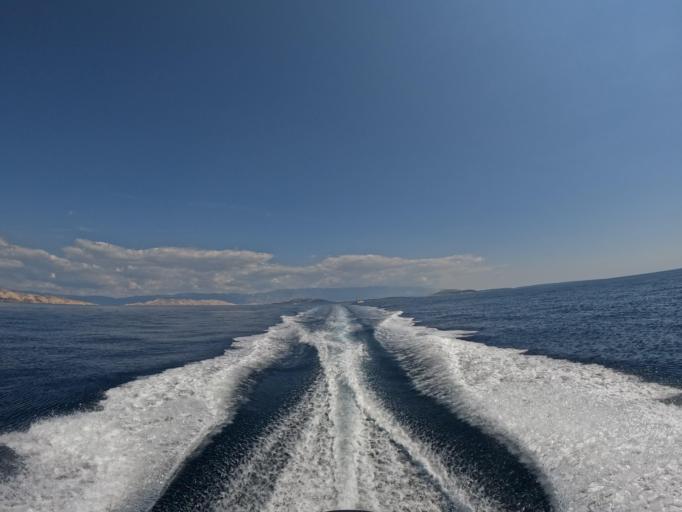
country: HR
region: Primorsko-Goranska
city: Punat
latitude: 44.9028
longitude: 14.6082
